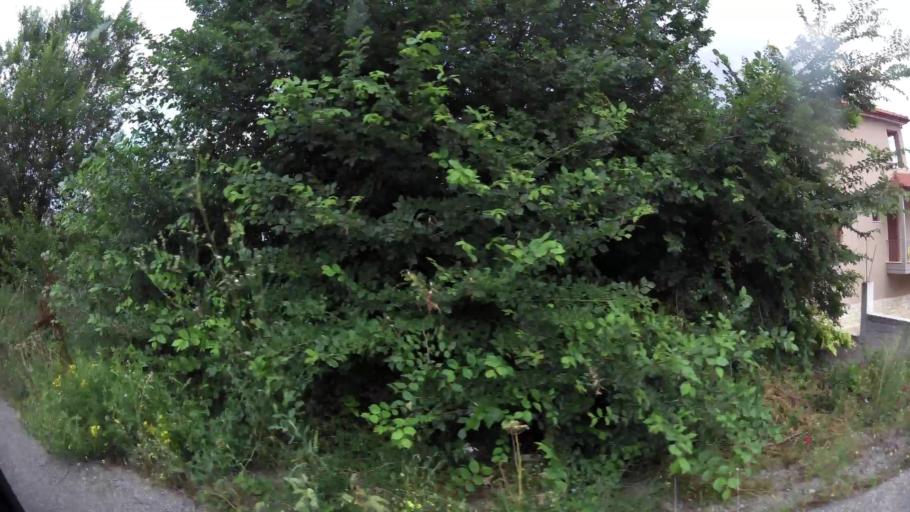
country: GR
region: West Macedonia
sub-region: Nomos Kozanis
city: Koila
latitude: 40.3480
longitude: 21.8222
